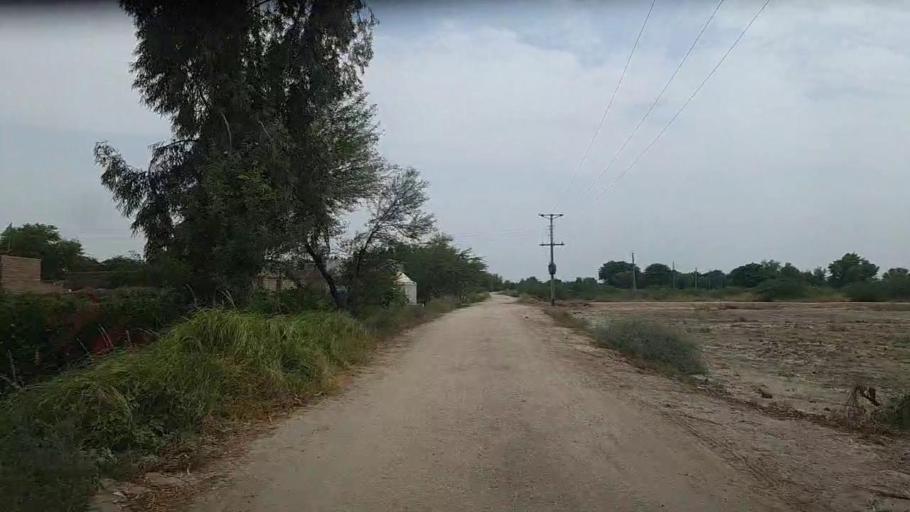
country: PK
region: Sindh
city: Bhiria
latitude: 26.8809
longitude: 68.2954
